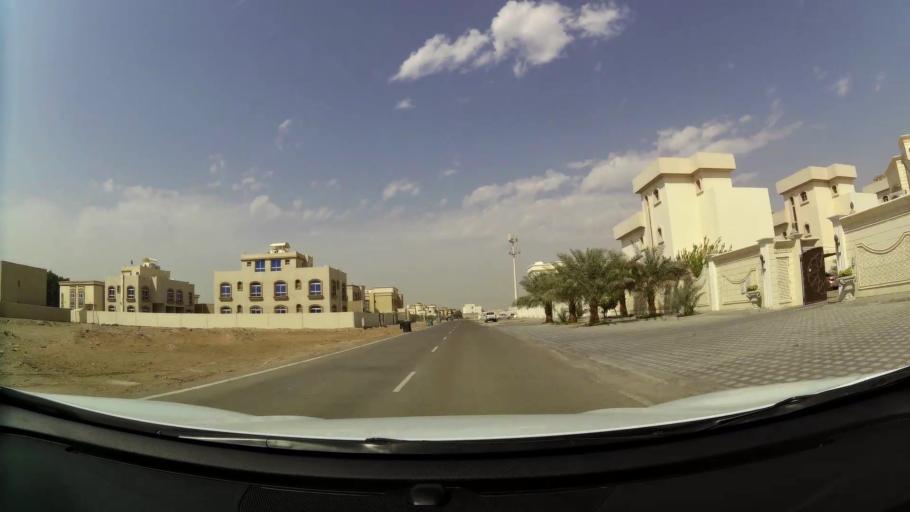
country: AE
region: Abu Dhabi
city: Abu Dhabi
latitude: 24.3283
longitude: 54.5461
